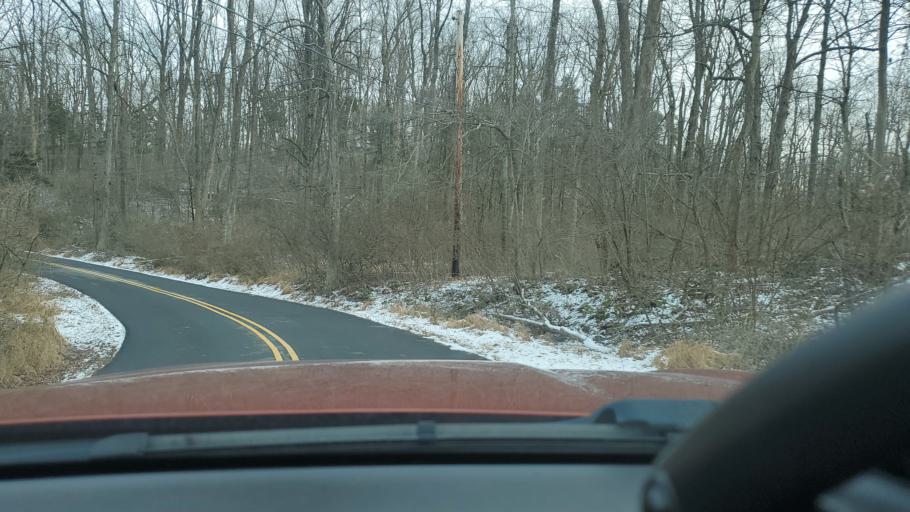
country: US
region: Pennsylvania
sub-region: Montgomery County
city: Red Hill
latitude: 40.3227
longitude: -75.5167
